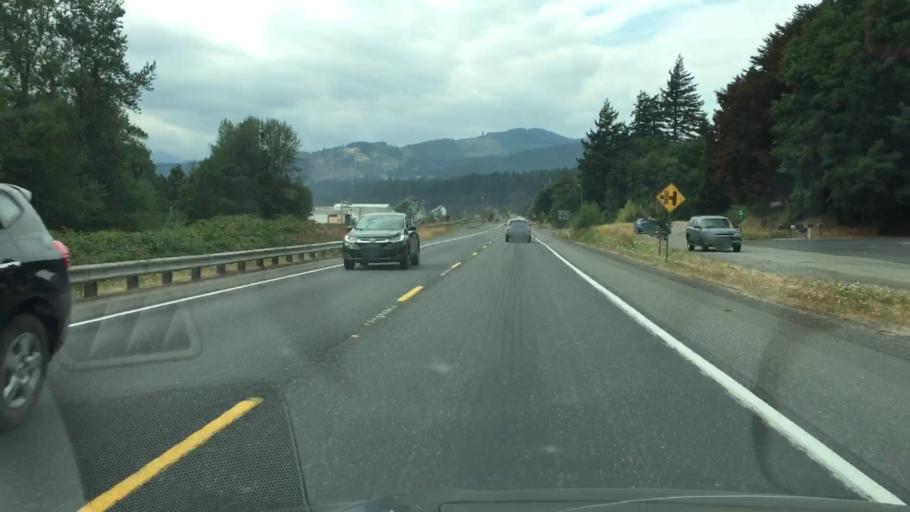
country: US
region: Washington
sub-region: Skamania County
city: Carson
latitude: 45.7109
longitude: -121.7761
